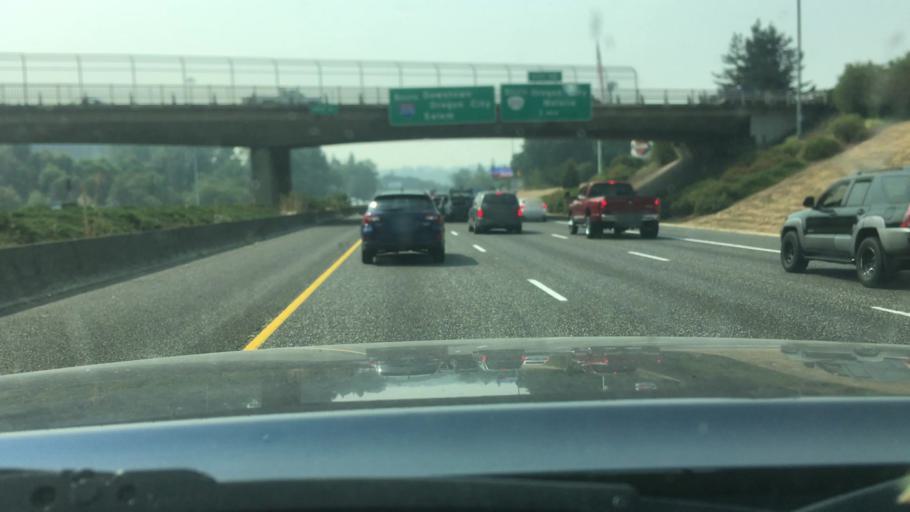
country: US
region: Oregon
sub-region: Clackamas County
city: Gladstone
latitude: 45.3853
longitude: -122.5790
